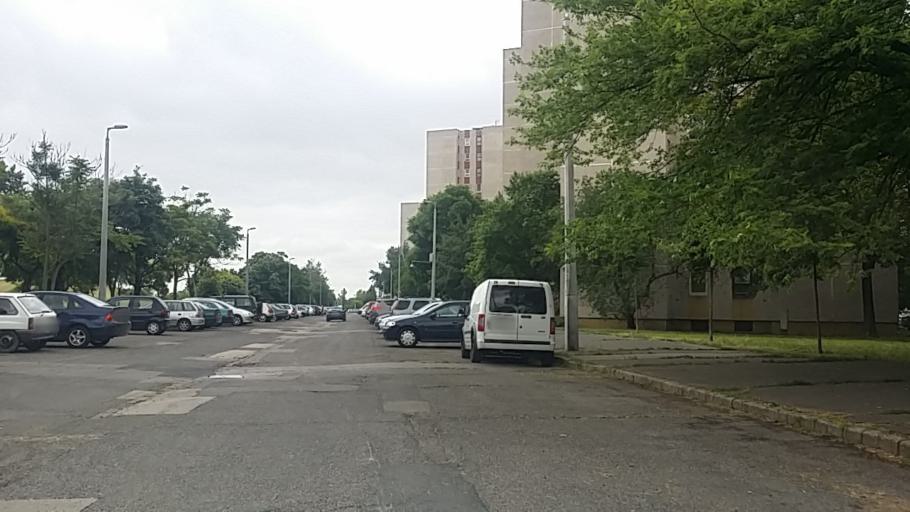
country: HU
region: Budapest
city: Budapest XX. keruelet
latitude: 47.4254
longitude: 19.0882
